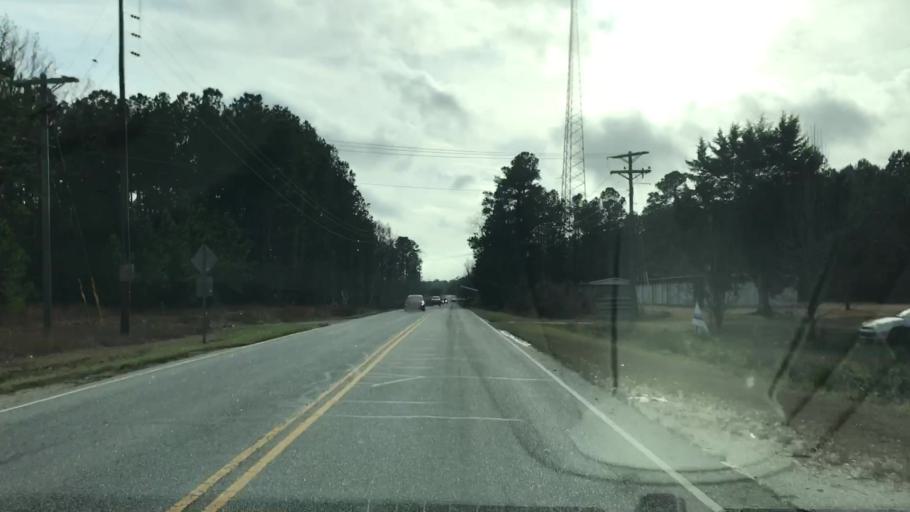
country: US
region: South Carolina
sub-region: Williamsburg County
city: Andrews
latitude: 33.3576
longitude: -79.6563
